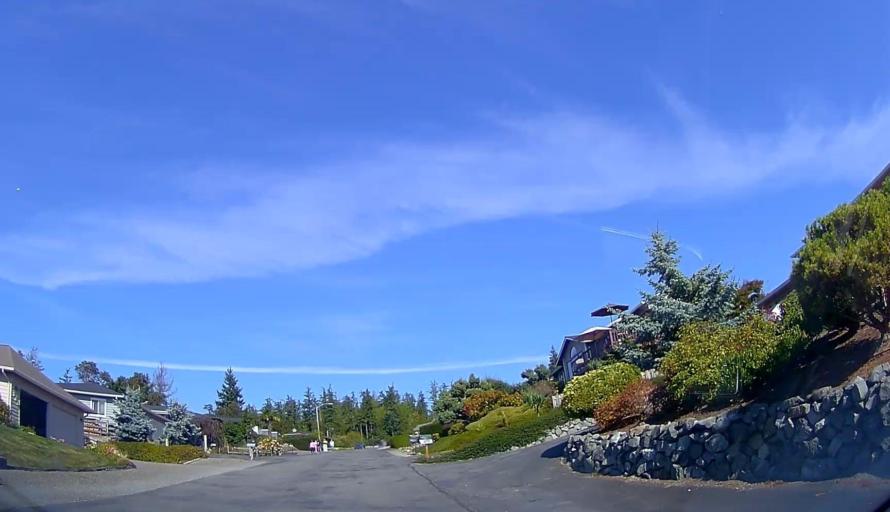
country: US
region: Washington
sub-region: Island County
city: Camano
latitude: 48.1832
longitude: -122.5344
